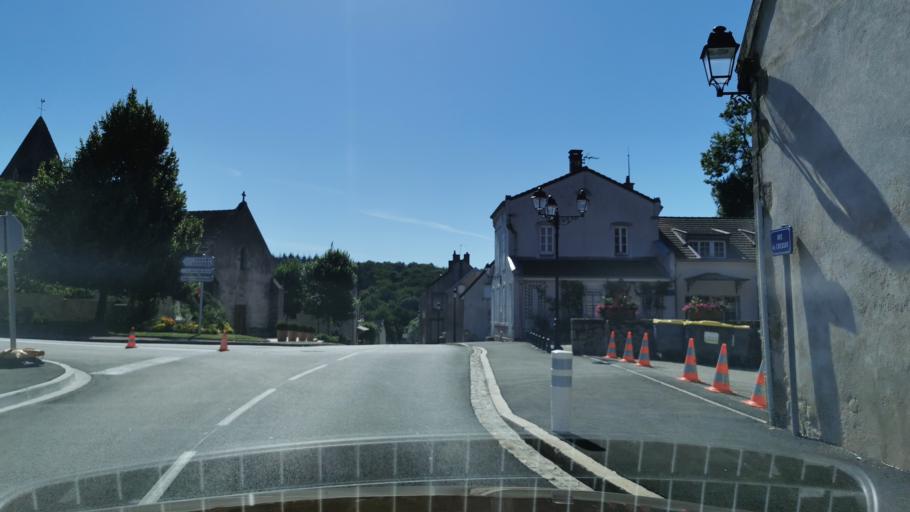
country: FR
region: Bourgogne
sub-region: Departement de Saone-et-Loire
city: Le Breuil
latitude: 46.7951
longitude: 4.4827
